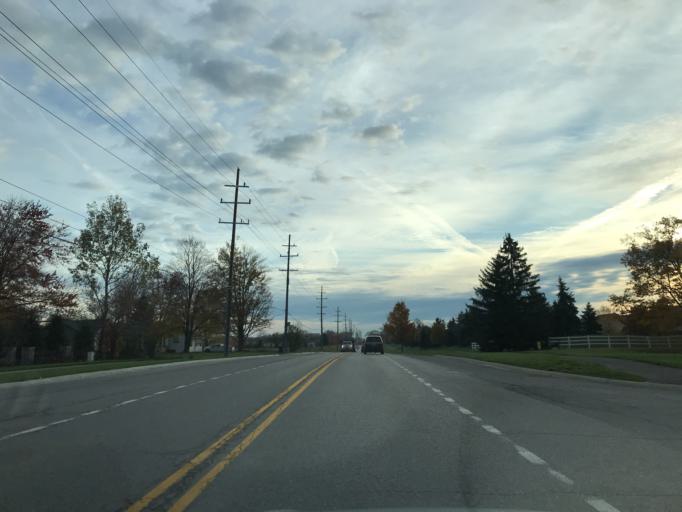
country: US
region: Michigan
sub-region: Oakland County
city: South Lyon
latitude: 42.4630
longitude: -83.5842
